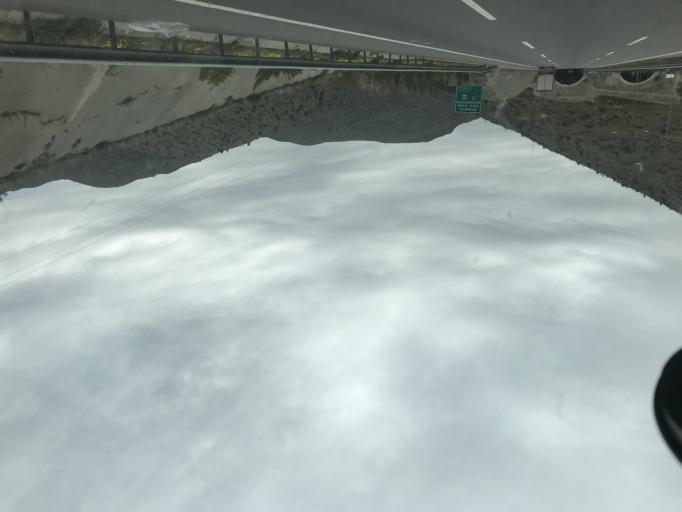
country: TR
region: Nigde
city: Ciftehan
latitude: 37.5717
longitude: 34.7538
